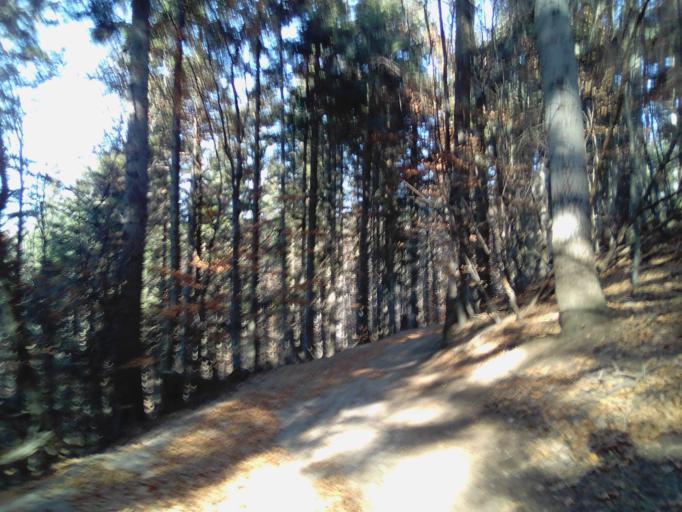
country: PL
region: Subcarpathian Voivodeship
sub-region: Powiat strzyzowski
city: Wysoka Strzyzowska
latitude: 49.8108
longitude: 21.7176
